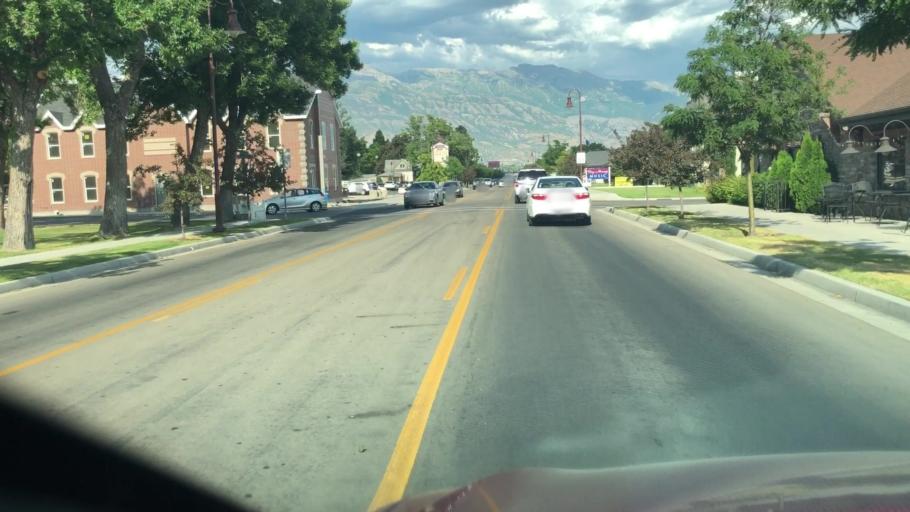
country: US
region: Utah
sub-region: Utah County
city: Lehi
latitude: 40.3878
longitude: -111.8480
